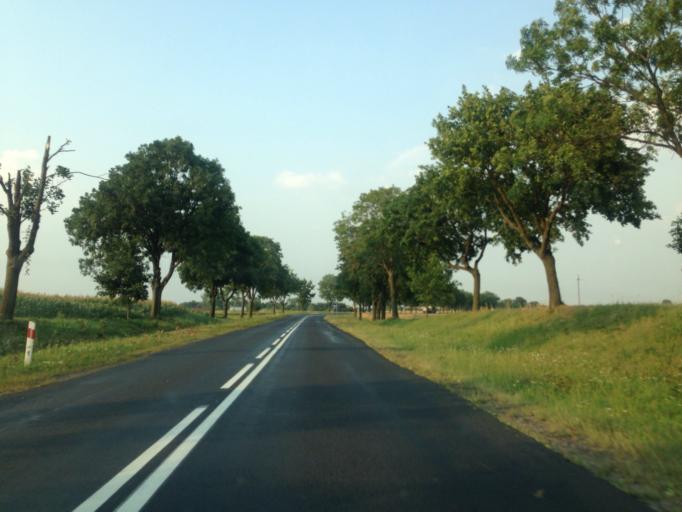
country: PL
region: Kujawsko-Pomorskie
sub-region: Powiat lipnowski
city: Chrostkowo
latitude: 52.9285
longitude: 19.2500
